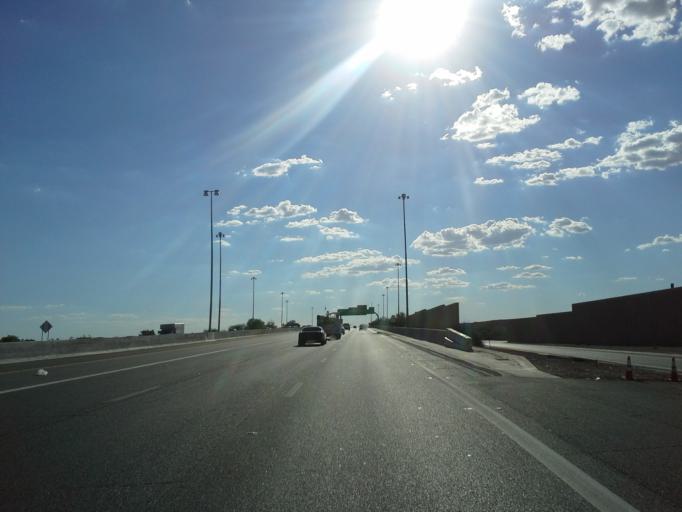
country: US
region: Arizona
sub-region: Maricopa County
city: Glendale
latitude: 33.6692
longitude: -112.0603
